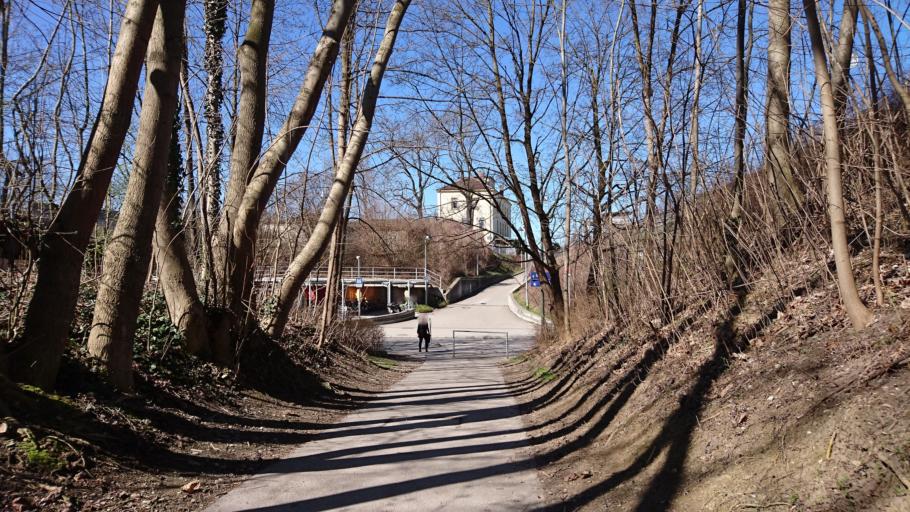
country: DE
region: Bavaria
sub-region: Swabia
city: Friedberg
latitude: 48.3529
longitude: 10.9455
